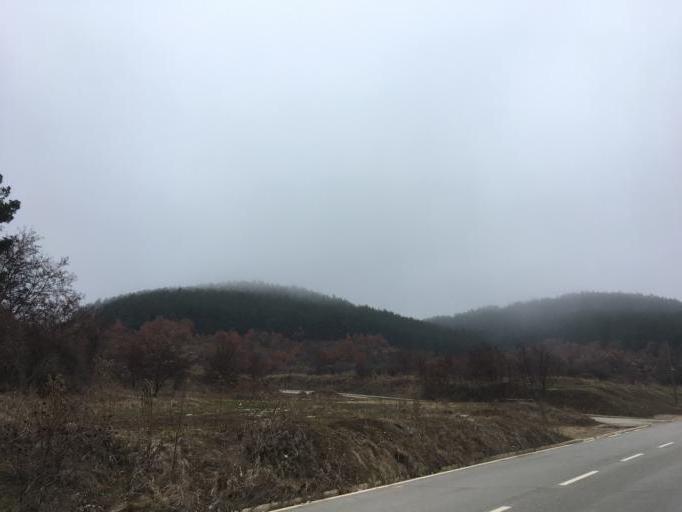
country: XK
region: Pristina
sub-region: Komuna e Prishtines
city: Pristina
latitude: 42.6731
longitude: 21.1979
